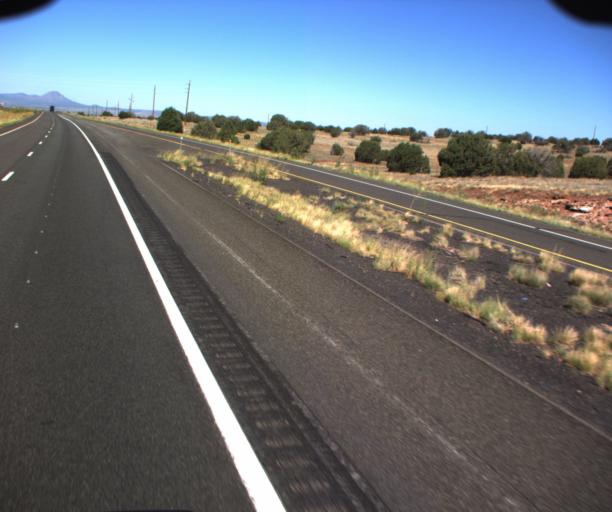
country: US
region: Arizona
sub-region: Coconino County
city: Williams
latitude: 35.2208
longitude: -112.5000
